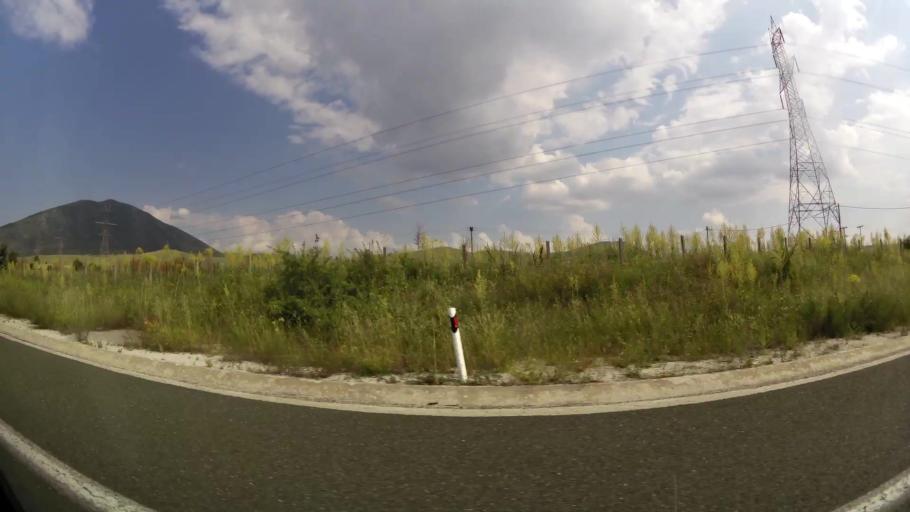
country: GR
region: West Macedonia
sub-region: Nomos Kozanis
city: Kleitos
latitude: 40.3622
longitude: 21.8551
